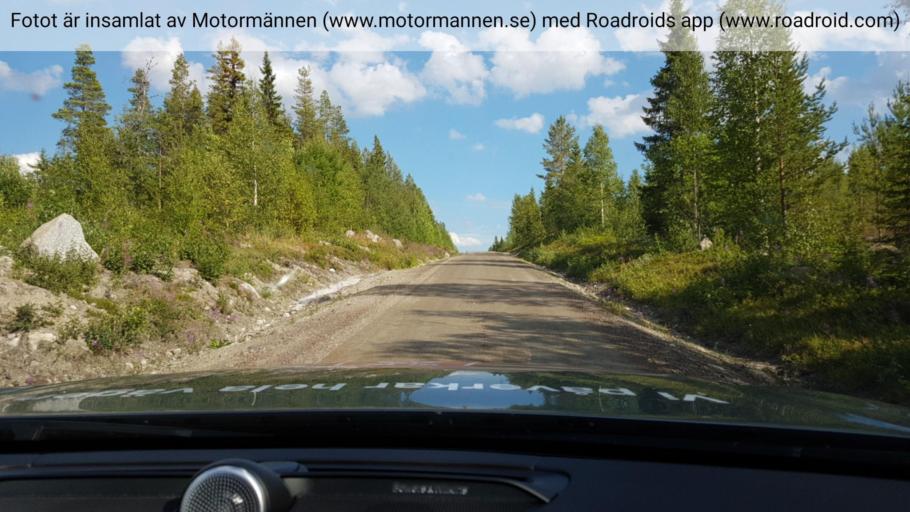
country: SE
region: Vaesterbotten
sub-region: Dorotea Kommun
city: Dorotea
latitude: 63.9306
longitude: 16.1152
